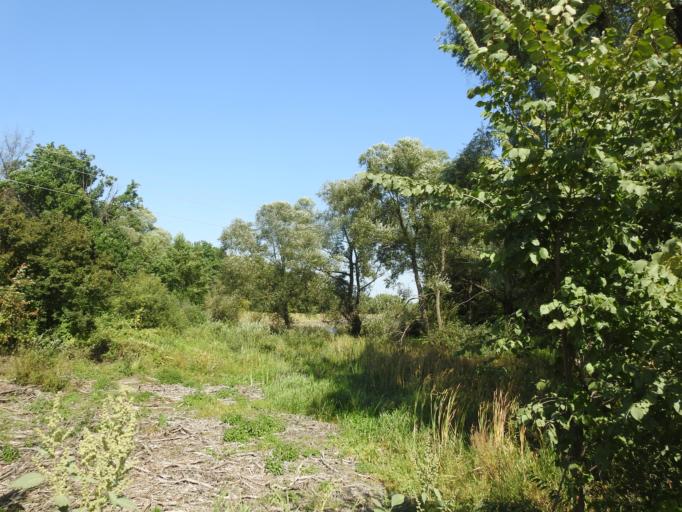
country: RU
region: Saratov
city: Lysyye Gory
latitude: 51.3114
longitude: 45.0139
